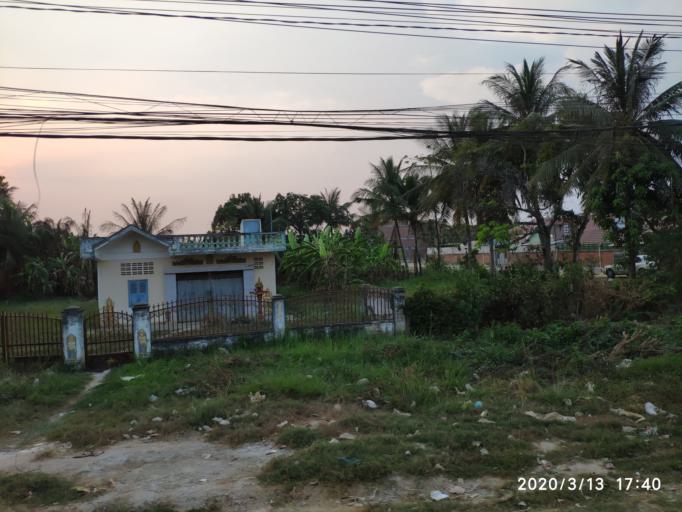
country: KH
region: Battambang
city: Battambang
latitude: 13.0808
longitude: 103.2148
